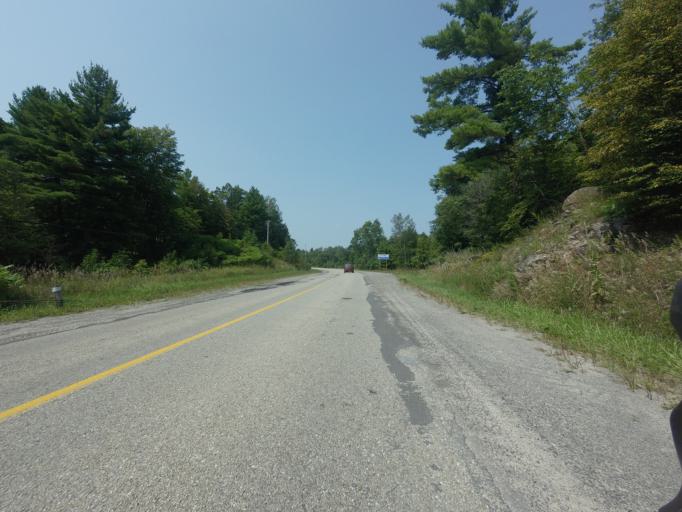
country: CA
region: Ontario
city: Perth
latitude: 44.6420
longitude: -76.5330
